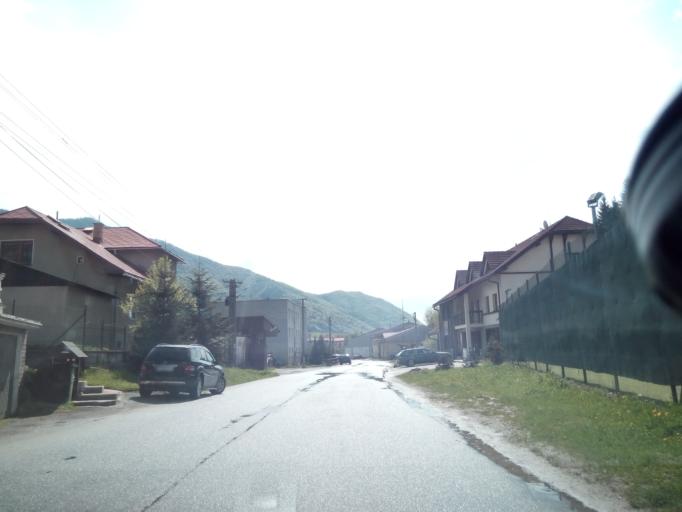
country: SK
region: Zilinsky
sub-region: Okres Zilina
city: Terchova
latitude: 49.2606
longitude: 19.0315
